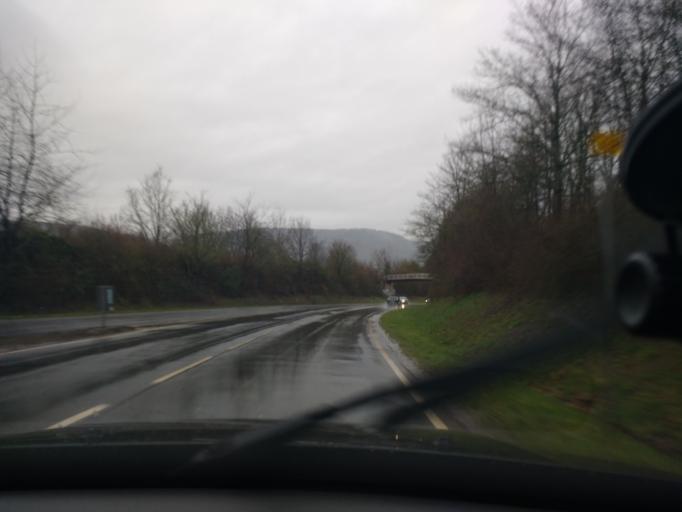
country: DE
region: Rheinland-Pfalz
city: Trier
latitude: 49.7248
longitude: 6.6279
